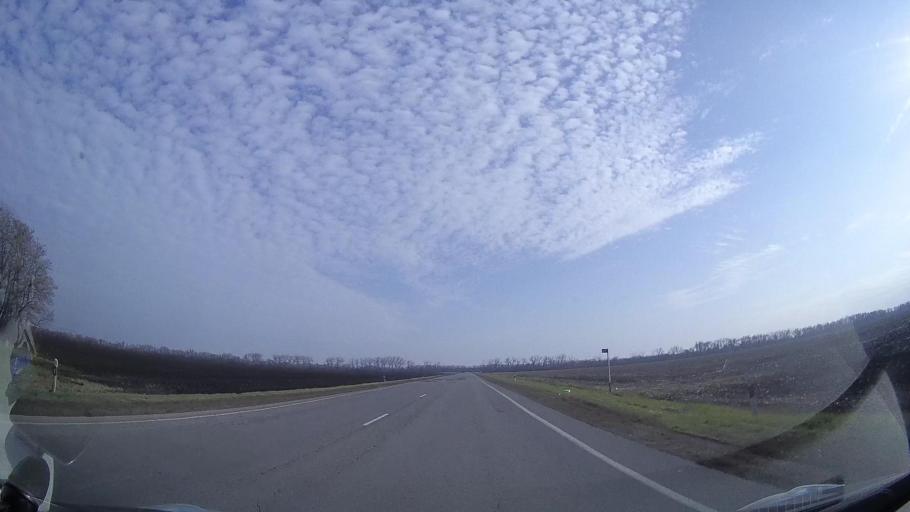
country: RU
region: Rostov
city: Tselina
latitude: 46.5218
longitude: 41.1433
